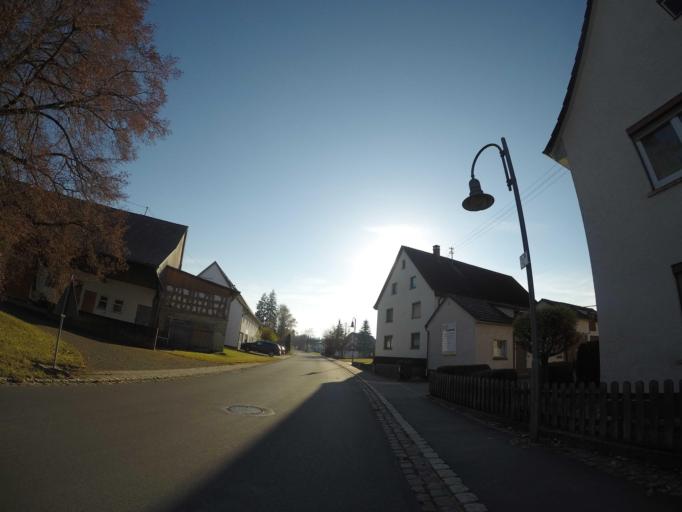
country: DE
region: Baden-Wuerttemberg
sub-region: Tuebingen Region
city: Emerkingen
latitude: 48.1929
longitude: 9.6636
